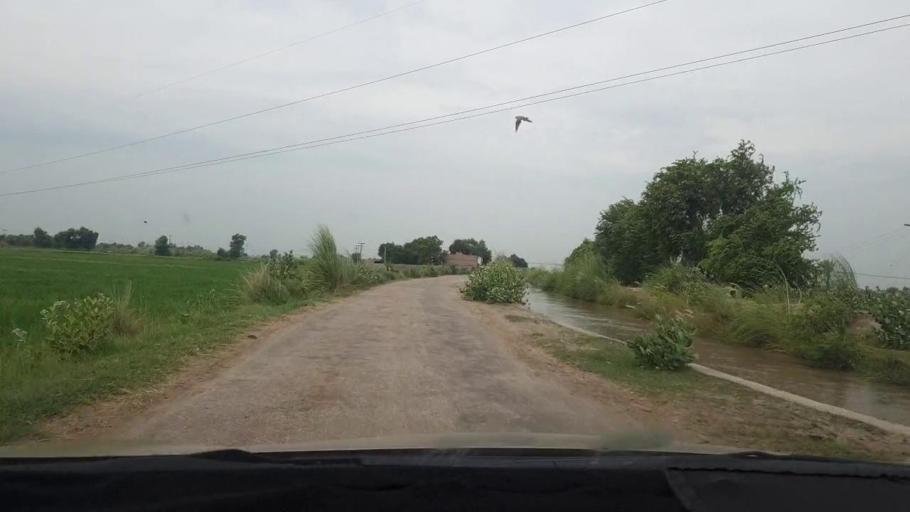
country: PK
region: Sindh
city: Naudero
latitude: 27.6793
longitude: 68.3461
